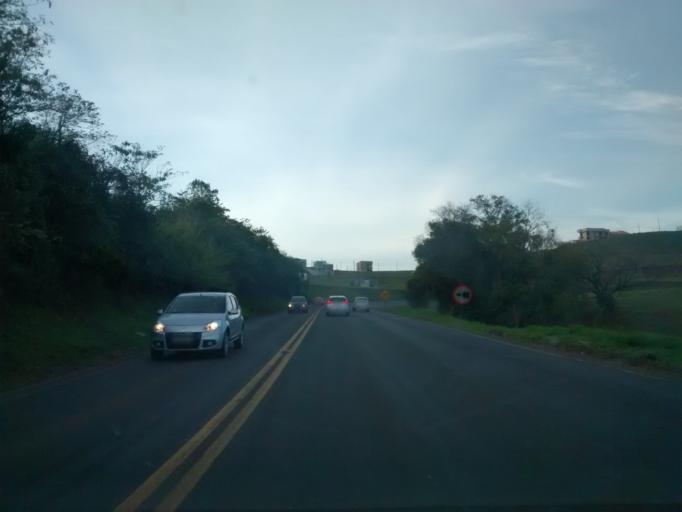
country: BR
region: Parana
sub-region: Francisco Beltrao
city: Francisco Beltrao
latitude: -26.1192
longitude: -53.0383
